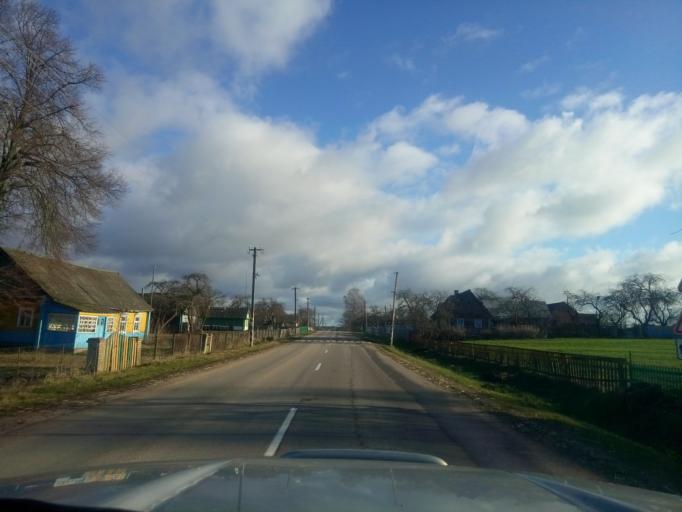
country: BY
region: Minsk
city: Tsimkavichy
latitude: 53.1759
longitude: 26.9518
